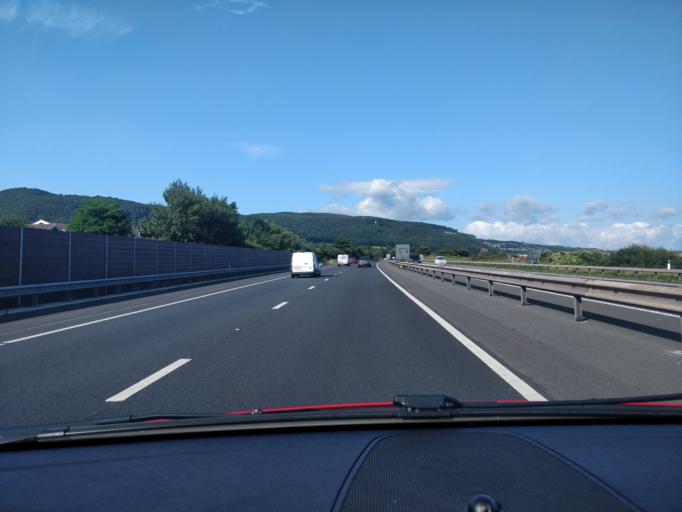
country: GB
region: Wales
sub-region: Conwy
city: Abergele
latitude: 53.2915
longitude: -3.5933
